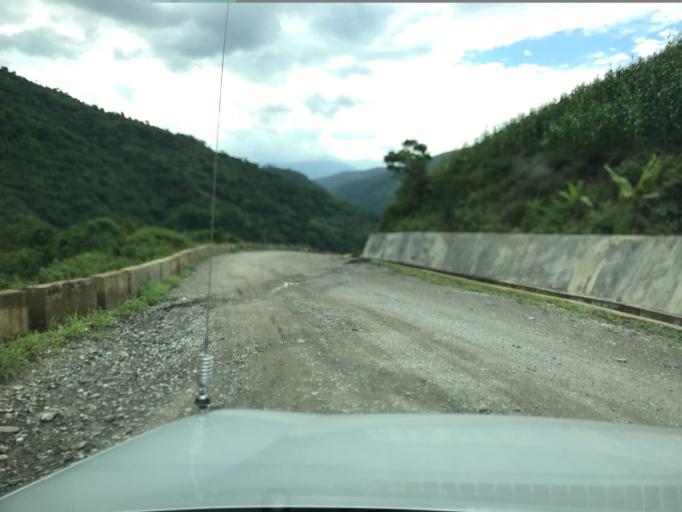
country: TL
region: Aileu
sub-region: Aileu Villa
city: Aileu
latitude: -8.6427
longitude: 125.5158
